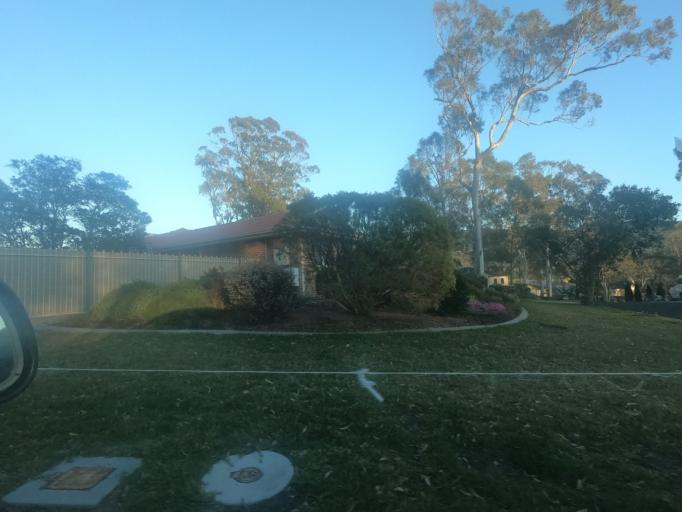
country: AU
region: New South Wales
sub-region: Wollongong
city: Dapto
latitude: -34.4928
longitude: 150.7646
